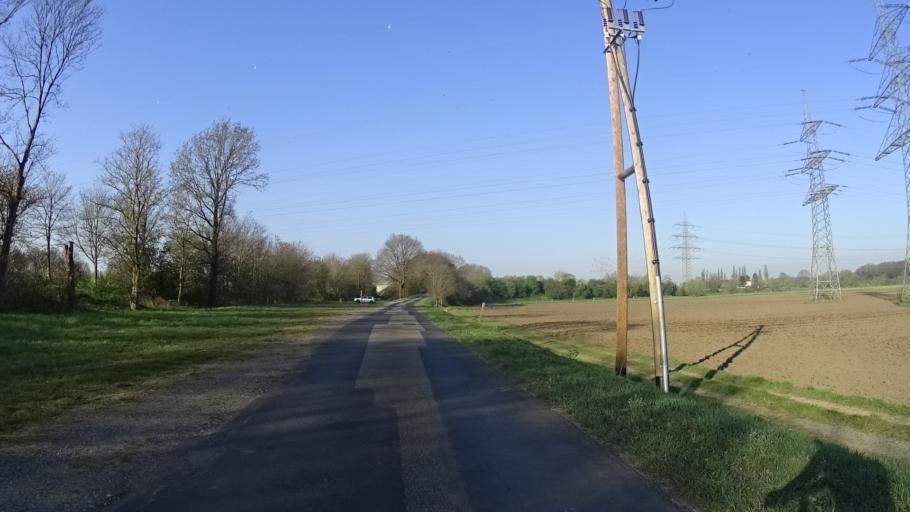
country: DE
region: North Rhine-Westphalia
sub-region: Regierungsbezirk Dusseldorf
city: Voerde
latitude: 51.6376
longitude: 6.6866
